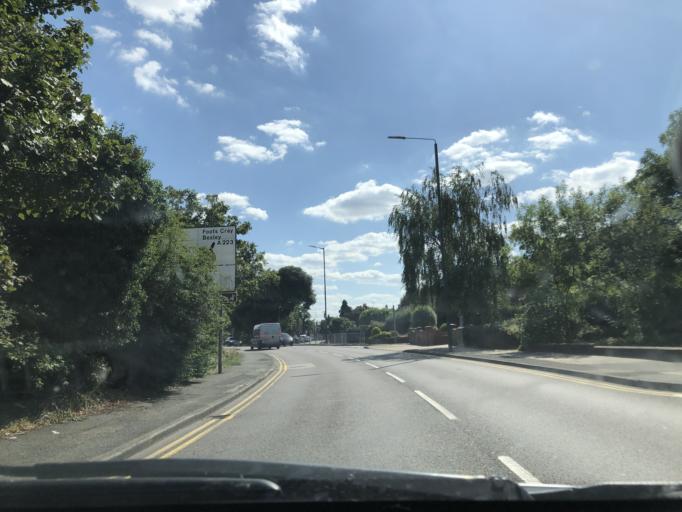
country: GB
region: England
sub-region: Greater London
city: Bexley
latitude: 51.4465
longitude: 0.1536
